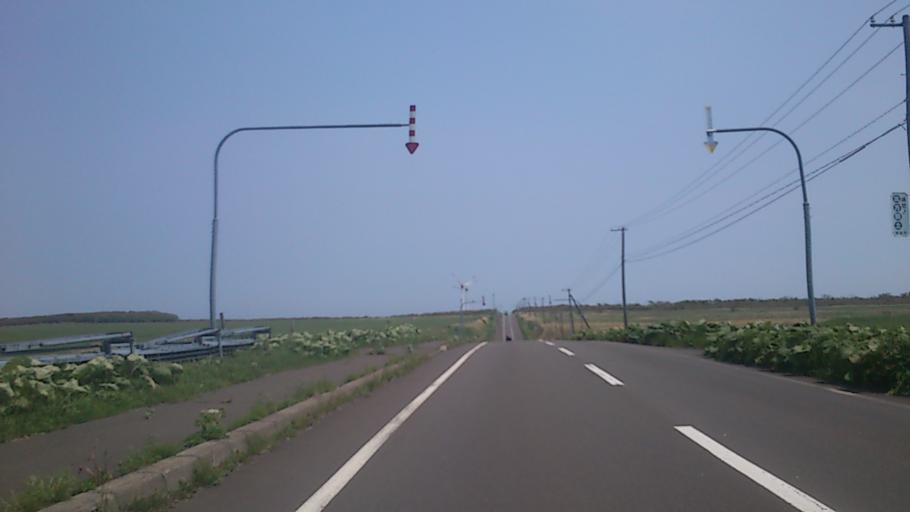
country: JP
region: Hokkaido
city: Nemuro
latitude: 43.3813
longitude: 145.6465
